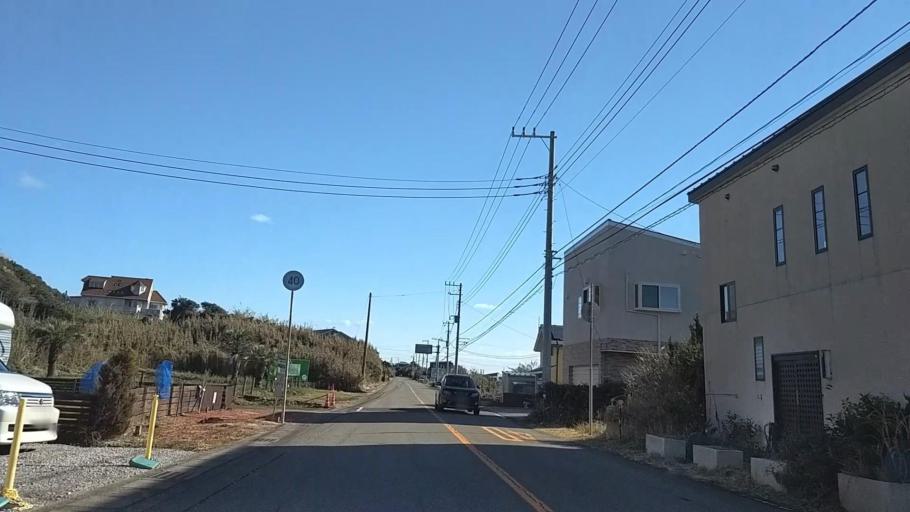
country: JP
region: Chiba
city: Tateyama
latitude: 34.9082
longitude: 139.8337
